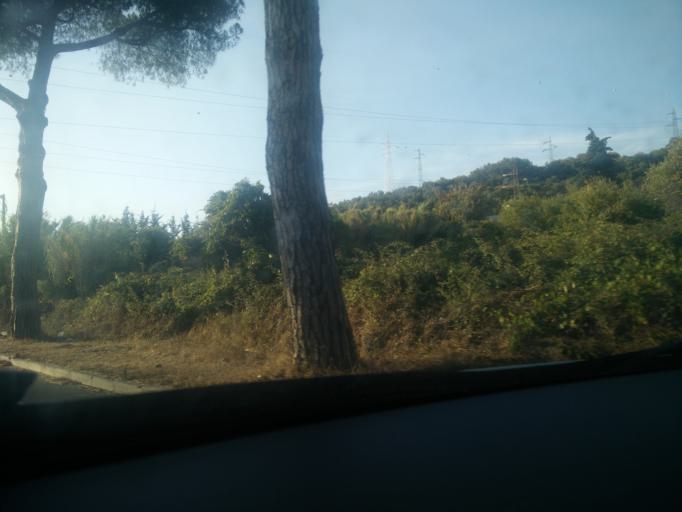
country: IT
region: Tuscany
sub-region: Provincia di Massa-Carrara
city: Carrara
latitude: 44.0466
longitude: 10.0805
